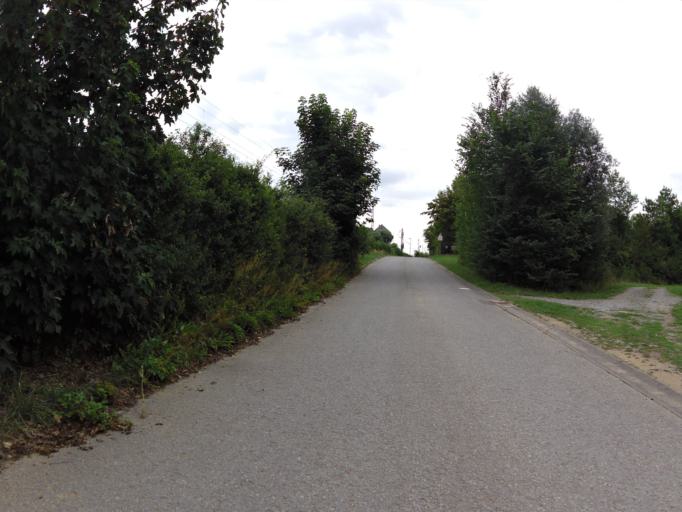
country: DE
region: Bavaria
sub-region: Regierungsbezirk Unterfranken
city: Gadheim
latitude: 50.0202
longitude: 10.3515
